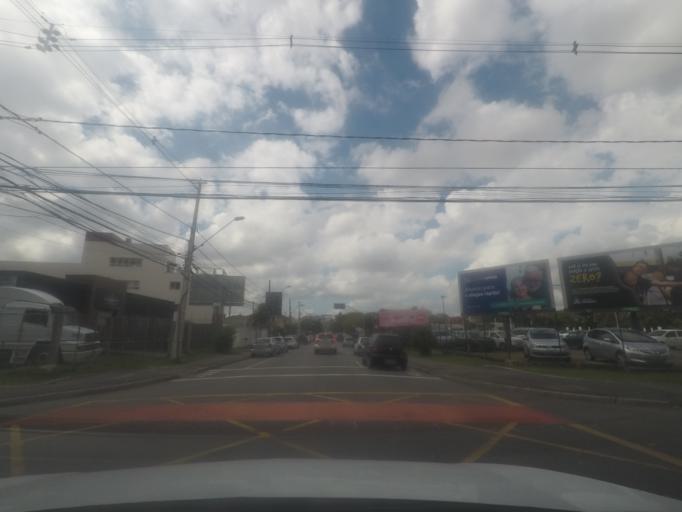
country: BR
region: Parana
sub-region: Curitiba
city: Curitiba
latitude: -25.4483
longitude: -49.2544
